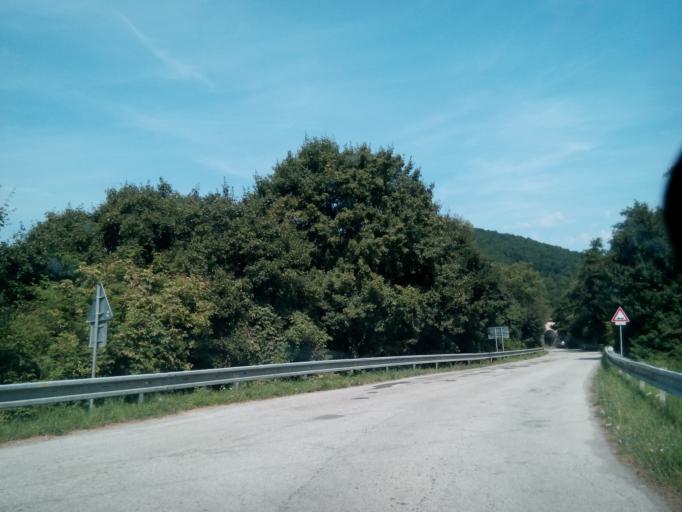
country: SK
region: Presovsky
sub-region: Okres Presov
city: Presov
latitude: 48.8573
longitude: 21.2267
